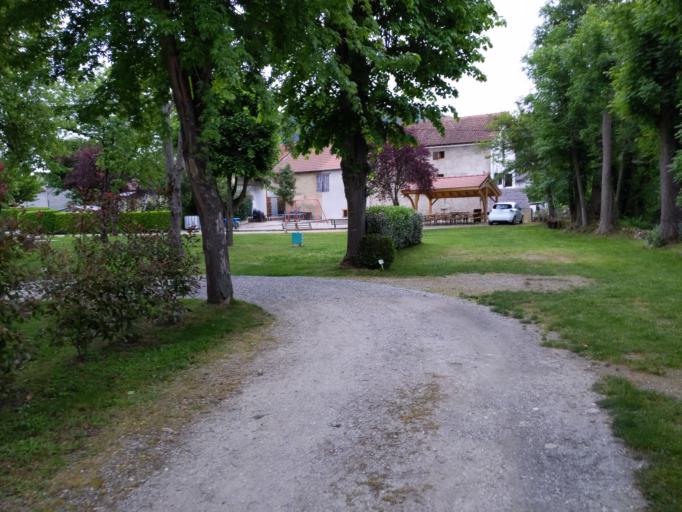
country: FR
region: Midi-Pyrenees
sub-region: Departement de l'Ariege
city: Tarascon-sur-Ariege
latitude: 42.8556
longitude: 1.5879
